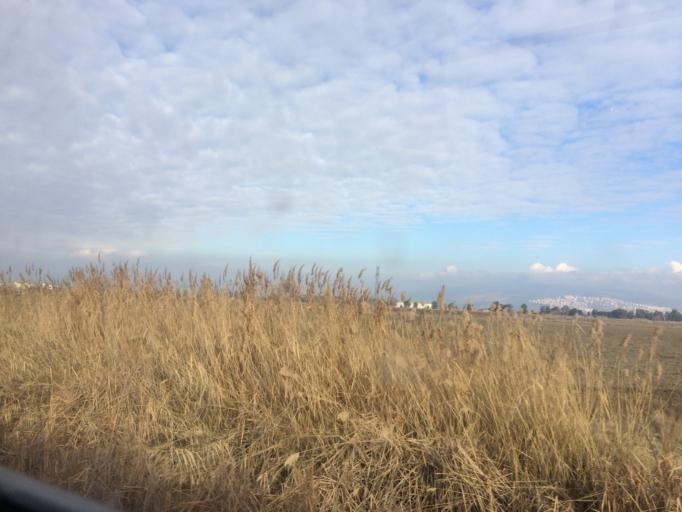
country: TR
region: Izmir
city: Menemen
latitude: 38.4973
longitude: 26.9602
